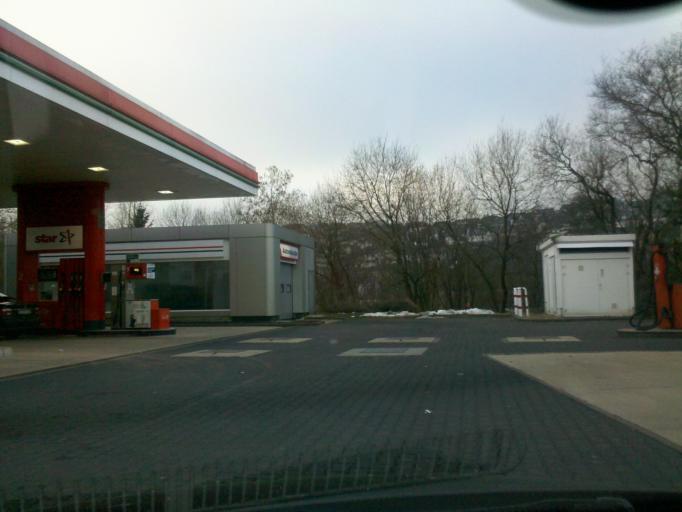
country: DE
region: North Rhine-Westphalia
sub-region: Regierungsbezirk Arnsberg
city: Olpe
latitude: 51.0192
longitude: 7.8417
